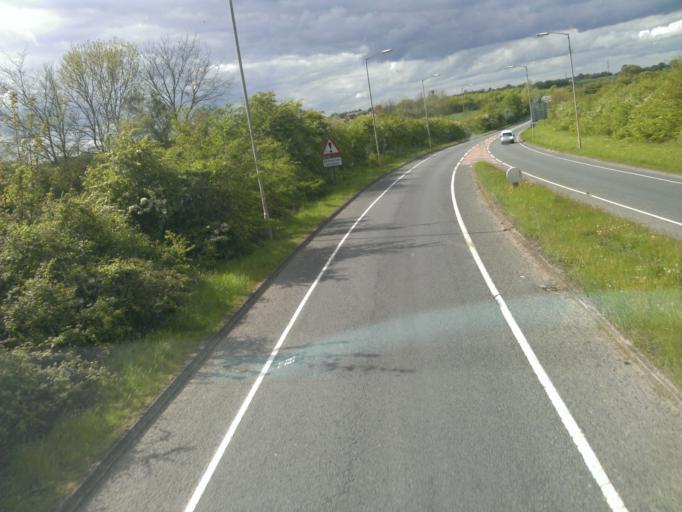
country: GB
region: England
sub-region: Essex
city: Coggeshall
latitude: 51.8740
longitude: 0.7015
